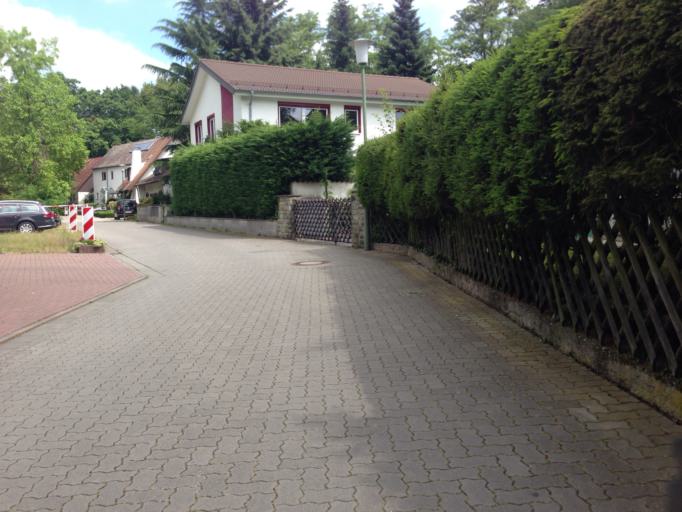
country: DE
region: Hesse
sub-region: Regierungsbezirk Darmstadt
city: Hanau am Main
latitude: 50.1418
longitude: 8.9221
